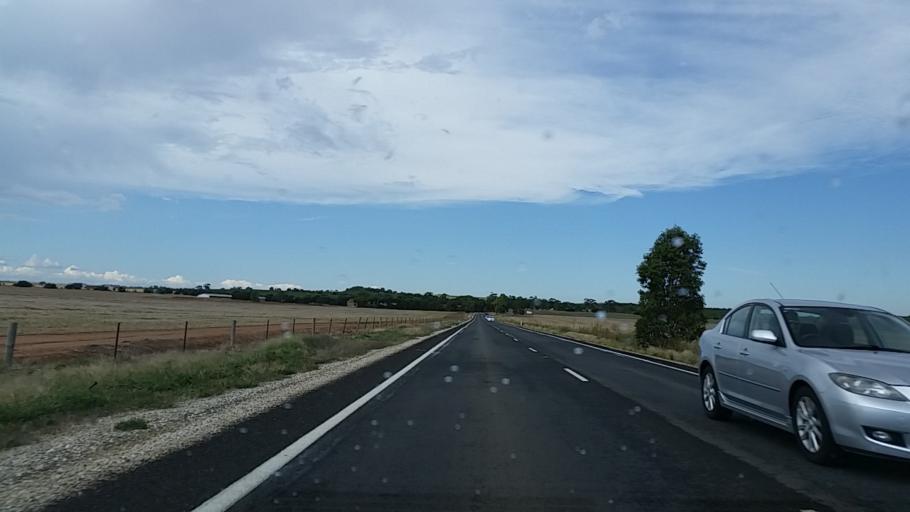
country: AU
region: South Australia
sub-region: Light
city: Freeling
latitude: -34.5228
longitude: 138.8303
